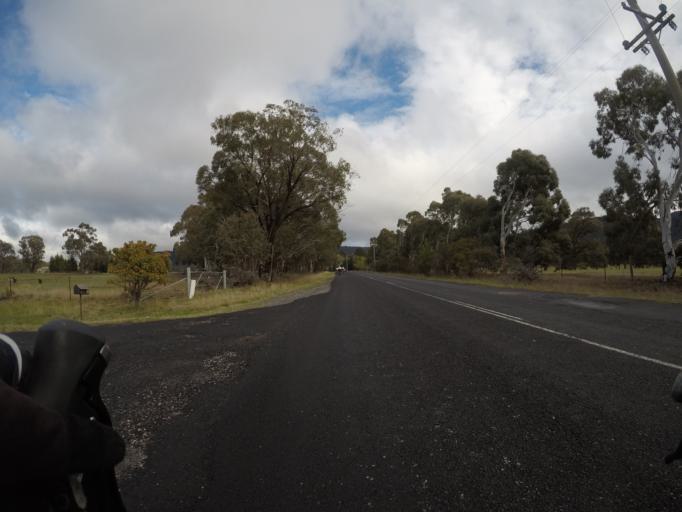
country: AU
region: New South Wales
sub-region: Lithgow
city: Lithgow
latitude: -33.5182
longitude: 150.1906
